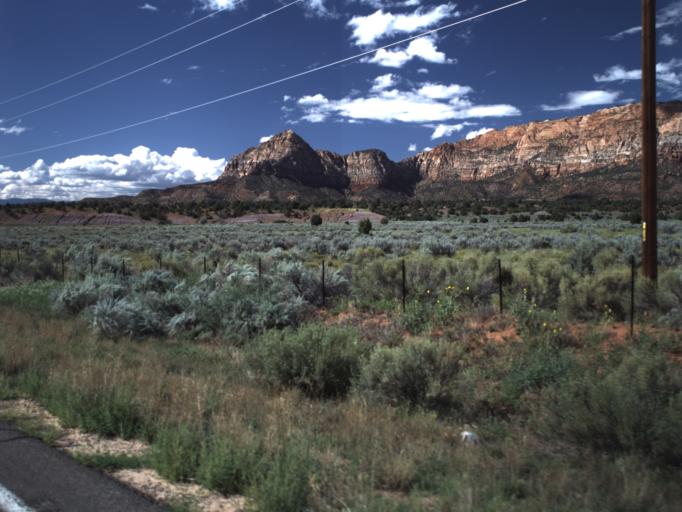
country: US
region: Arizona
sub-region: Mohave County
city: Colorado City
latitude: 37.0160
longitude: -113.0266
